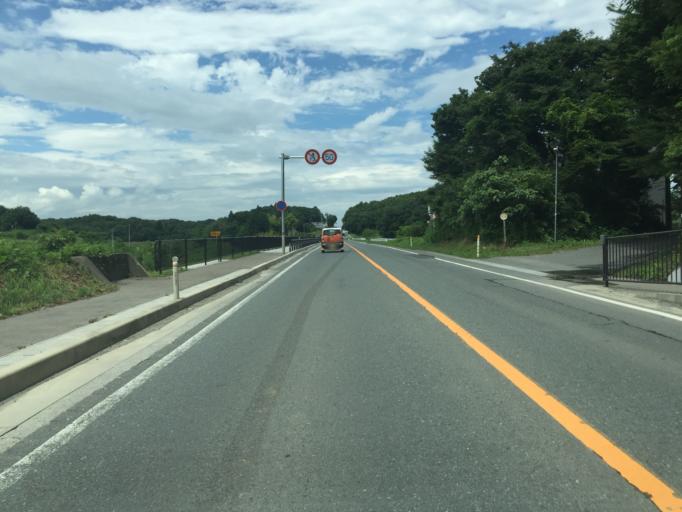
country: JP
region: Fukushima
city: Namie
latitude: 37.7323
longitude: 140.9535
